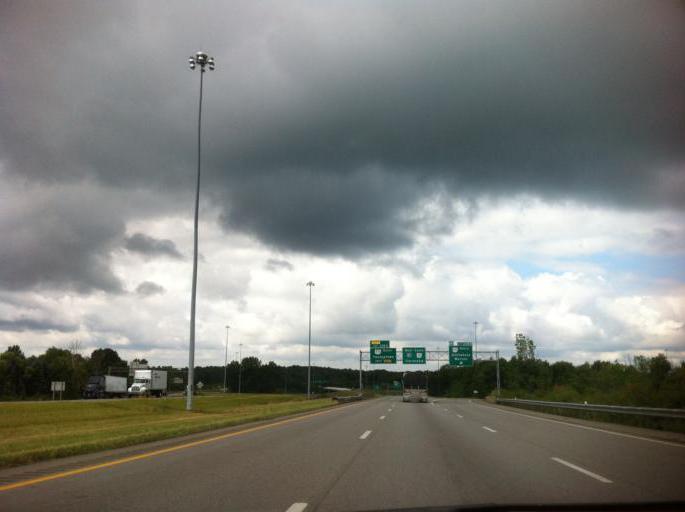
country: US
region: Ohio
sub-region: Trumbull County
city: Churchill
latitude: 41.1530
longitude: -80.6691
